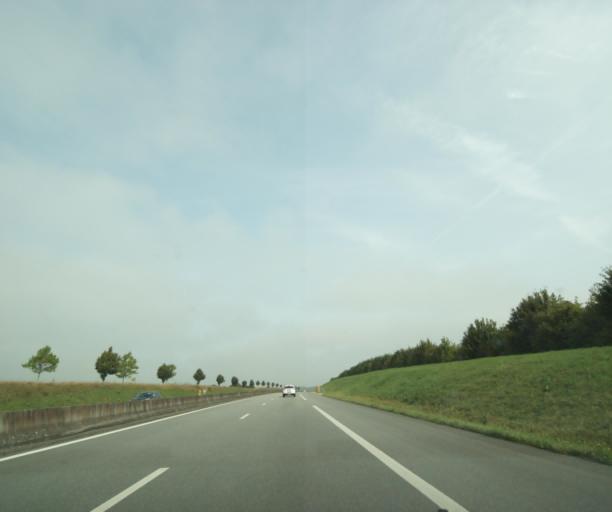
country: FR
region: Lower Normandy
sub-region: Departement de l'Orne
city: Sees
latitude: 48.5671
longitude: 0.1751
